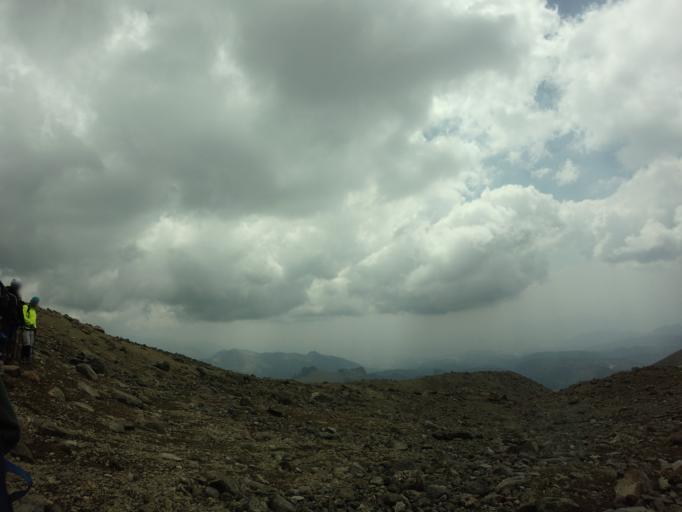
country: MX
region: Mexico
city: Amecameca de Juarez
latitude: 19.1657
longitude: -98.6460
